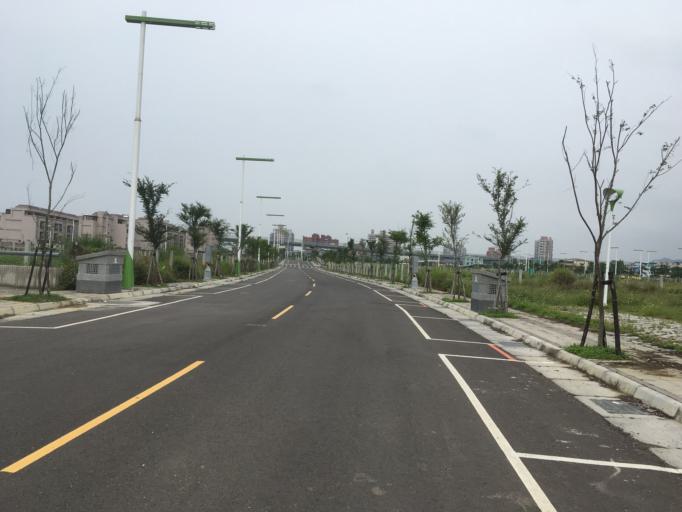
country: TW
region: Taiwan
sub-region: Taichung City
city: Taichung
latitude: 24.1937
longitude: 120.7061
